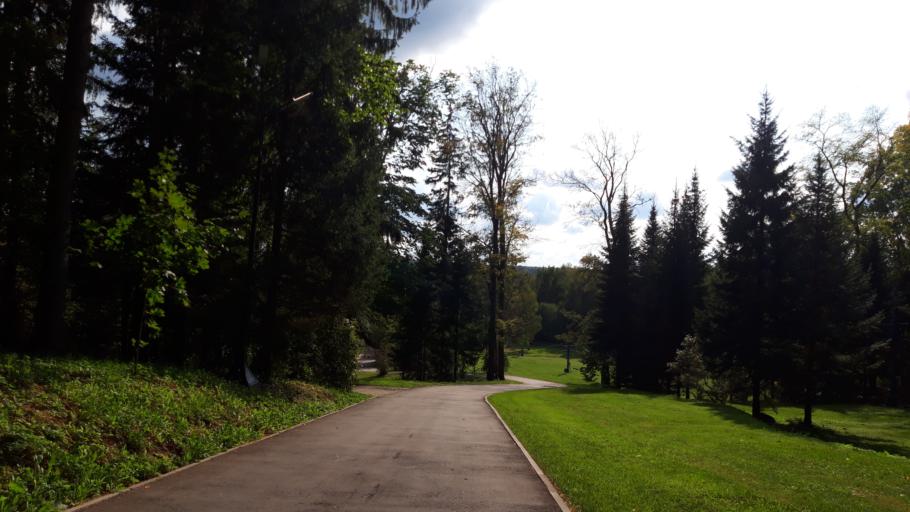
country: RU
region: Moskovskaya
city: Mendeleyevo
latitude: 56.0496
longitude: 37.2192
